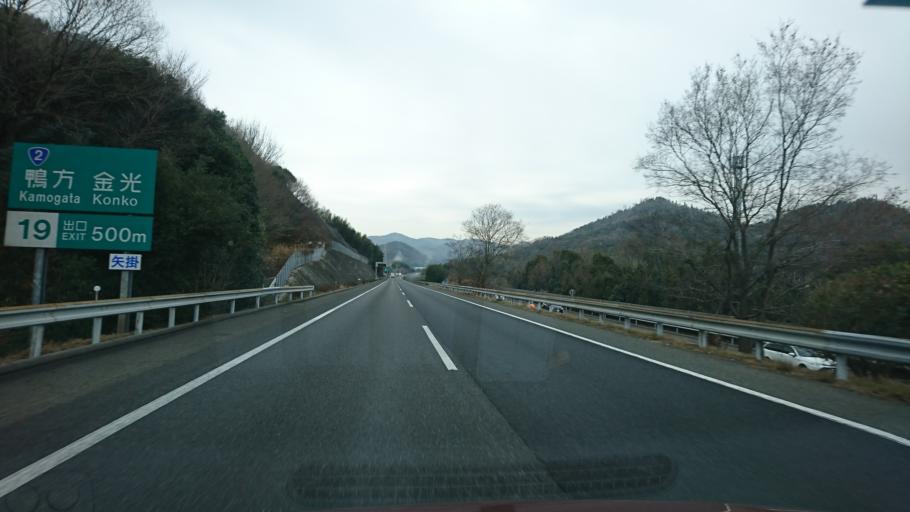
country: JP
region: Okayama
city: Kamogatacho-kamogata
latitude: 34.5528
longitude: 133.6002
